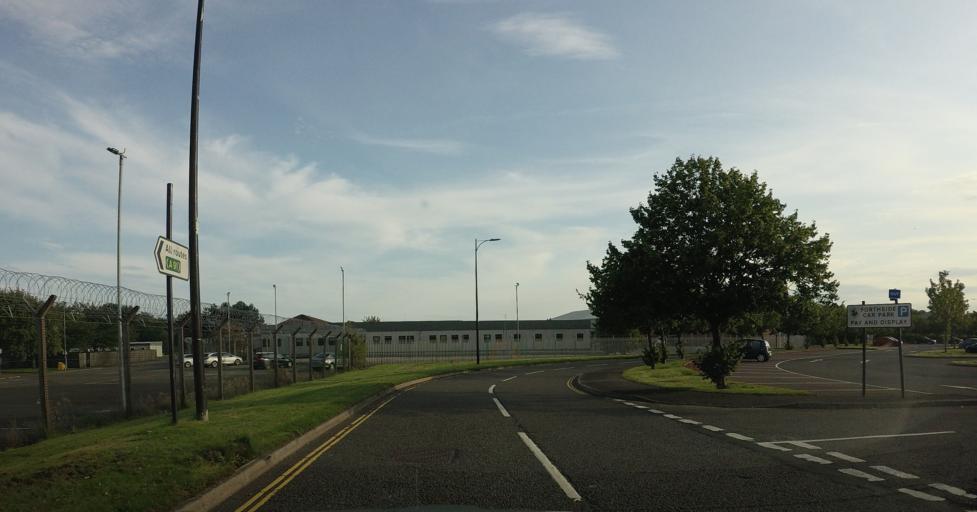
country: GB
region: Scotland
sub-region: Stirling
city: Stirling
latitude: 56.1178
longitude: -3.9268
